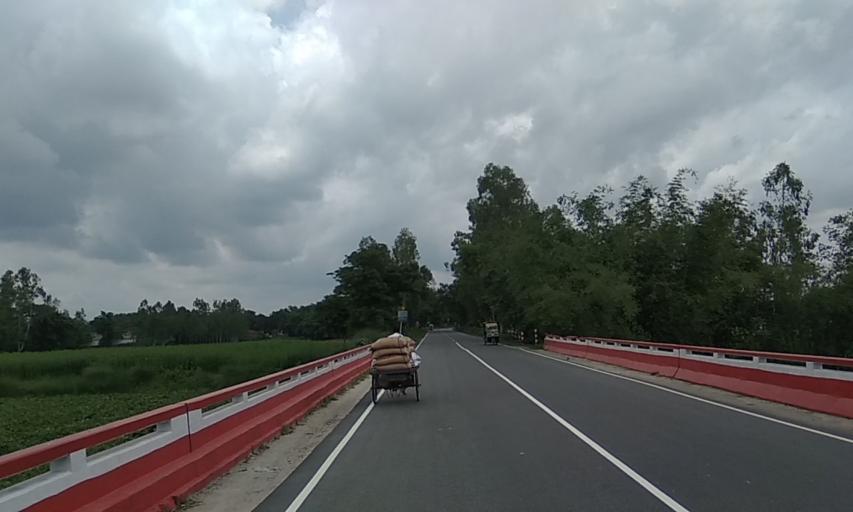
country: BD
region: Rangpur Division
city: Rangpur
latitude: 25.8017
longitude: 89.1848
